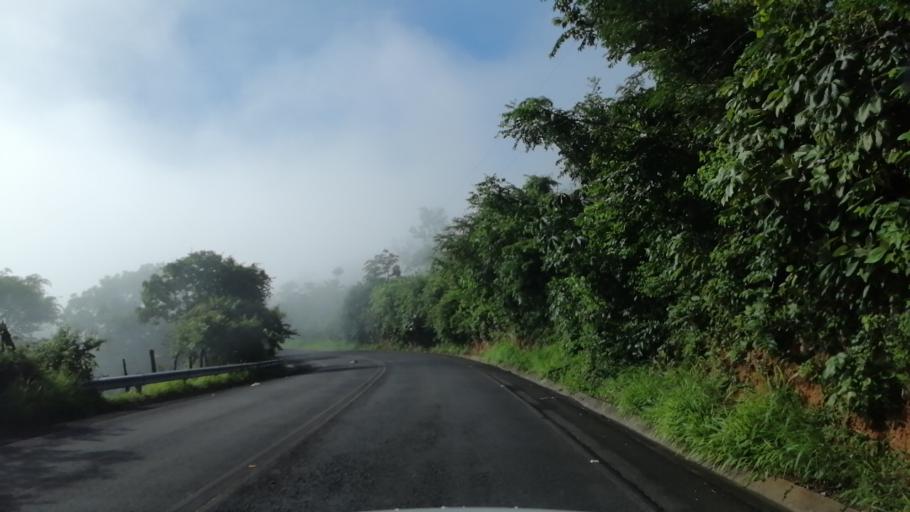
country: SV
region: Morazan
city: Cacaopera
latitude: 13.7917
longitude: -88.1215
